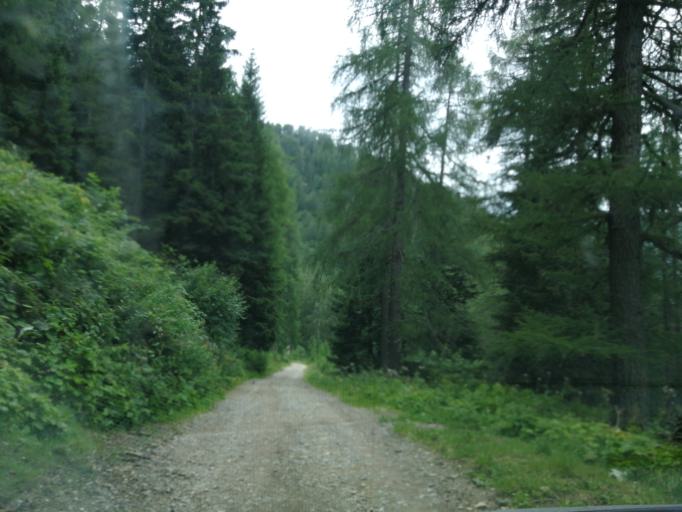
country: IT
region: Trentino-Alto Adige
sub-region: Provincia di Trento
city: Castel Condino
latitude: 45.9408
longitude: 10.5720
